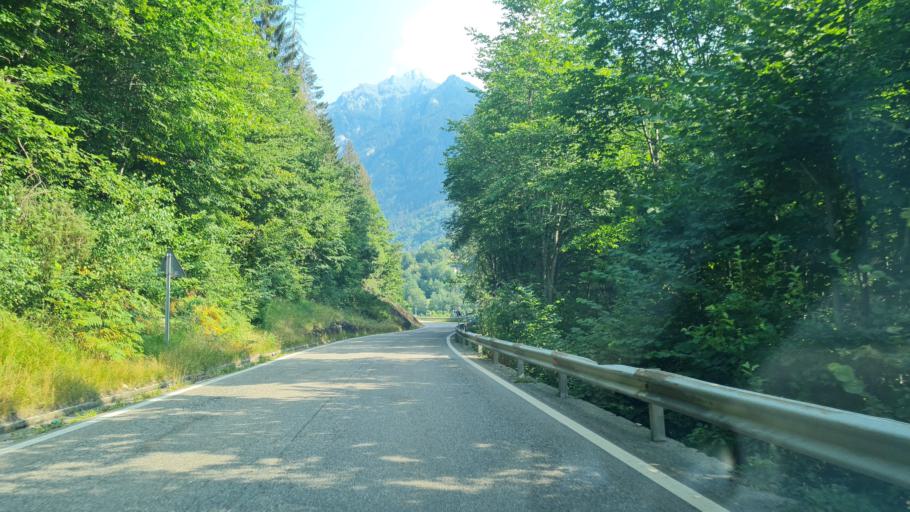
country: IT
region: Piedmont
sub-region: Provincia Verbano-Cusio-Ossola
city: Baceno
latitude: 46.2495
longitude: 8.3235
